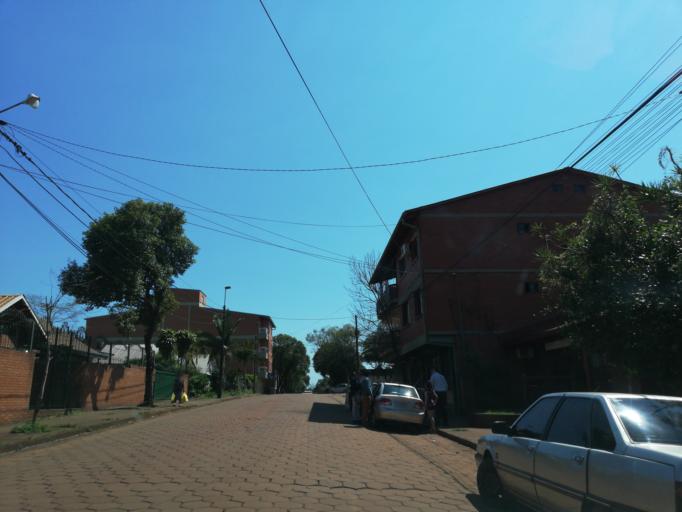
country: AR
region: Misiones
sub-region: Departamento de Eldorado
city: Eldorado
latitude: -26.4108
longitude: -54.6099
